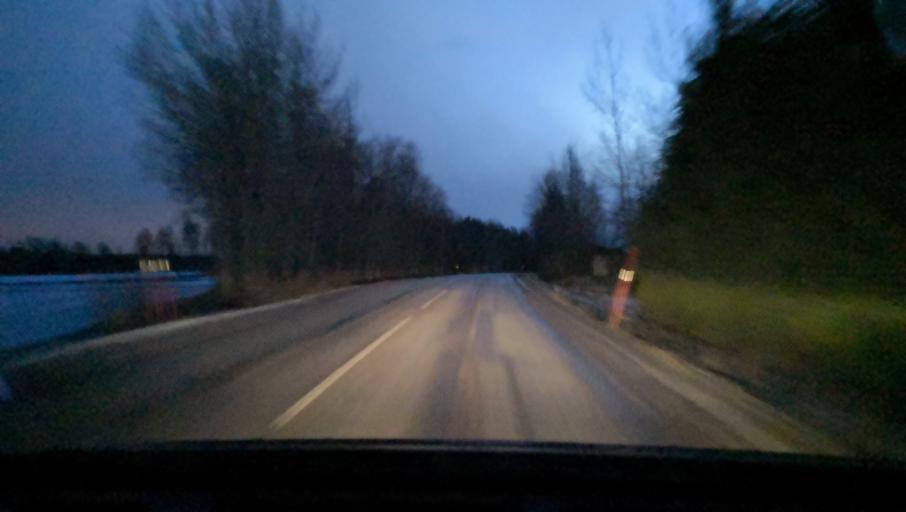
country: SE
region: Vaestmanland
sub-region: Vasteras
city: Skultuna
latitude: 59.7635
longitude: 16.4617
